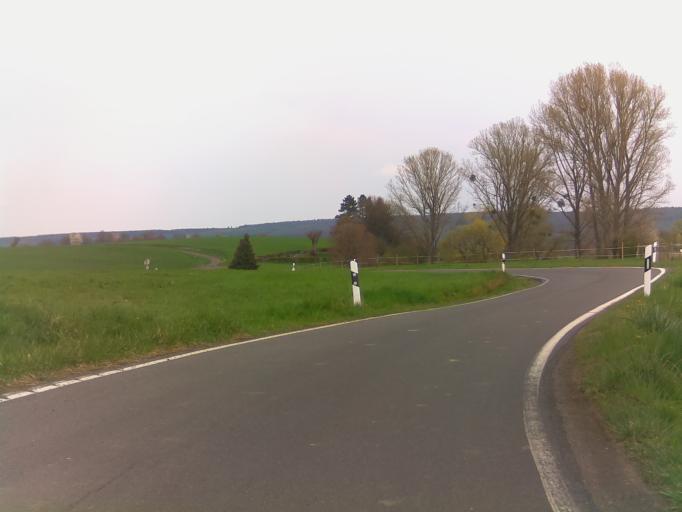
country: DE
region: Rheinland-Pfalz
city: Daubach
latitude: 49.8570
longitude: 7.6356
